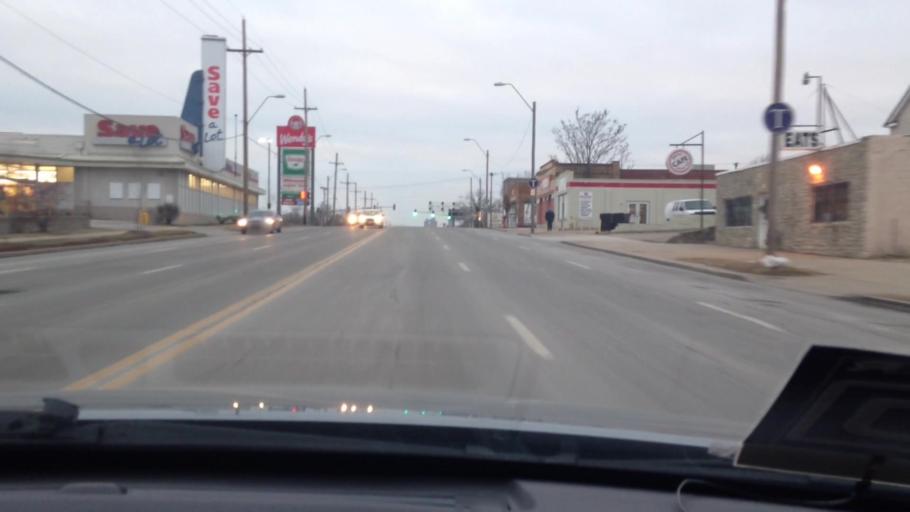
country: US
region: Missouri
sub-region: Jackson County
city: Kansas City
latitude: 39.0942
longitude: -94.5357
